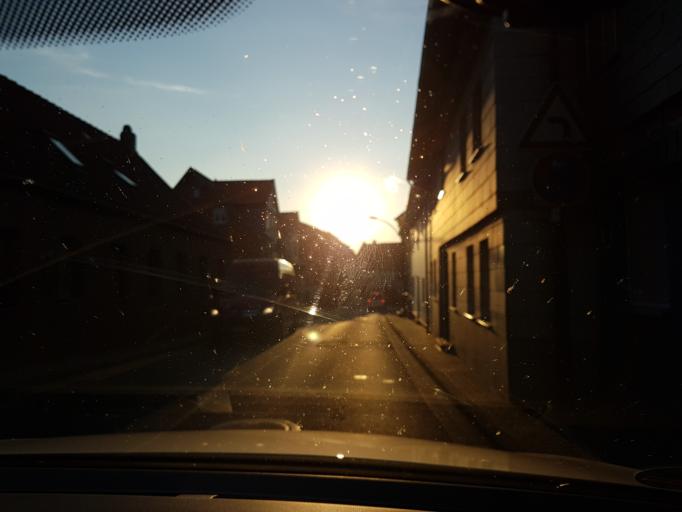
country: DE
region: Lower Saxony
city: Schoningen
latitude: 52.1391
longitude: 10.9582
